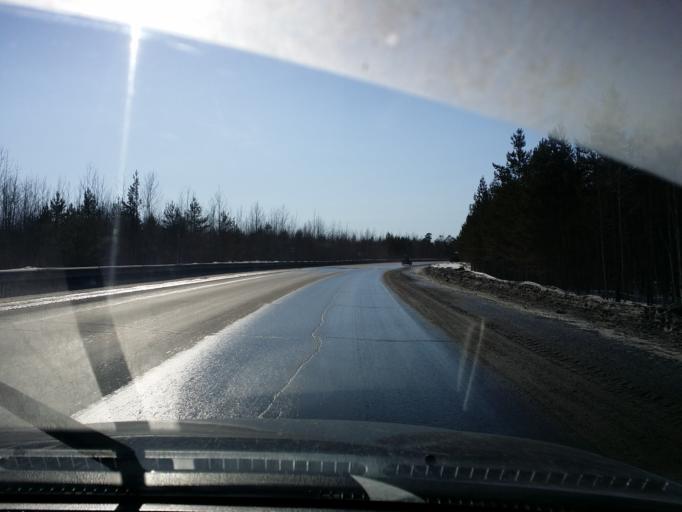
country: RU
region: Khanty-Mansiyskiy Avtonomnyy Okrug
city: Langepas
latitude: 61.1780
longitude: 75.5066
